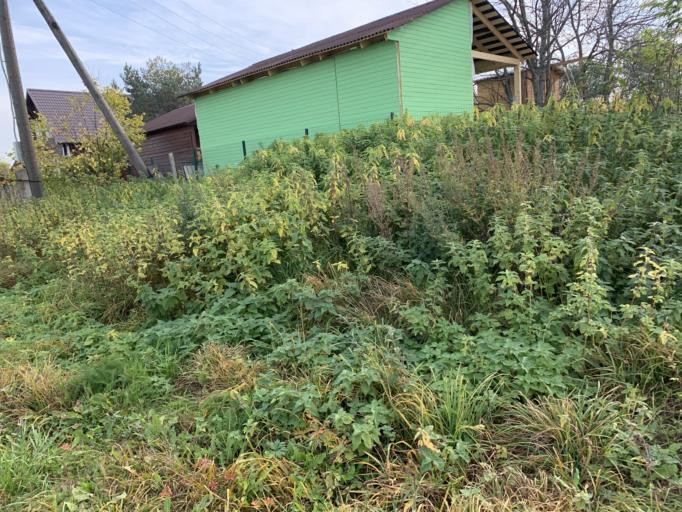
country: RU
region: Jaroslavl
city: Porech'ye-Rybnoye
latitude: 56.9812
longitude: 39.3850
